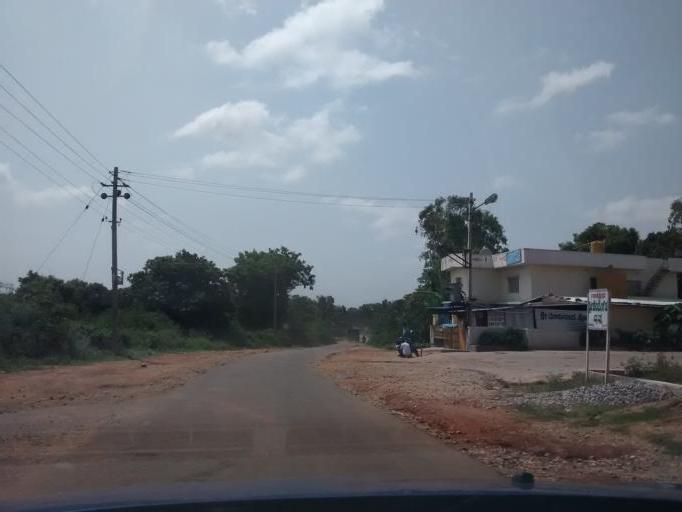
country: IN
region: Karnataka
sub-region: Hassan
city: Hole Narsipur
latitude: 12.7012
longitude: 76.1613
